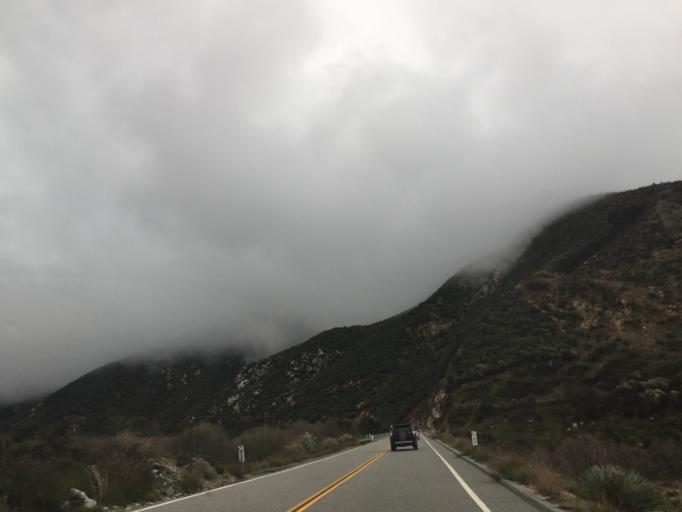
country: US
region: California
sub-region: Los Angeles County
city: Glendora
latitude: 34.2785
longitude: -117.8444
